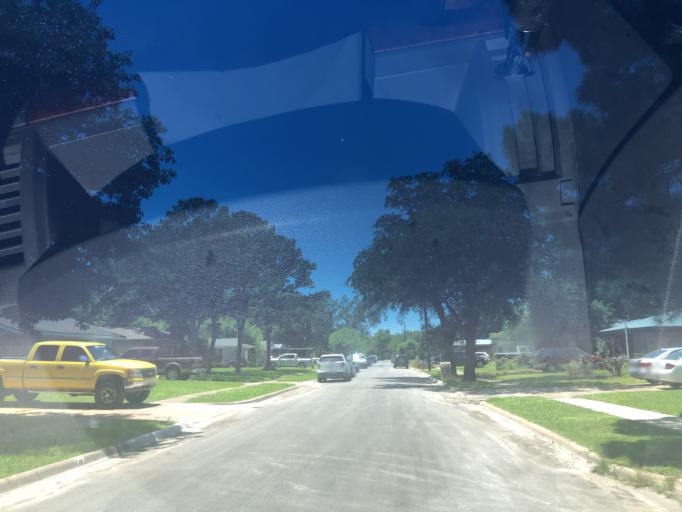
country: US
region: Texas
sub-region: Dallas County
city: Grand Prairie
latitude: 32.7168
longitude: -97.0034
